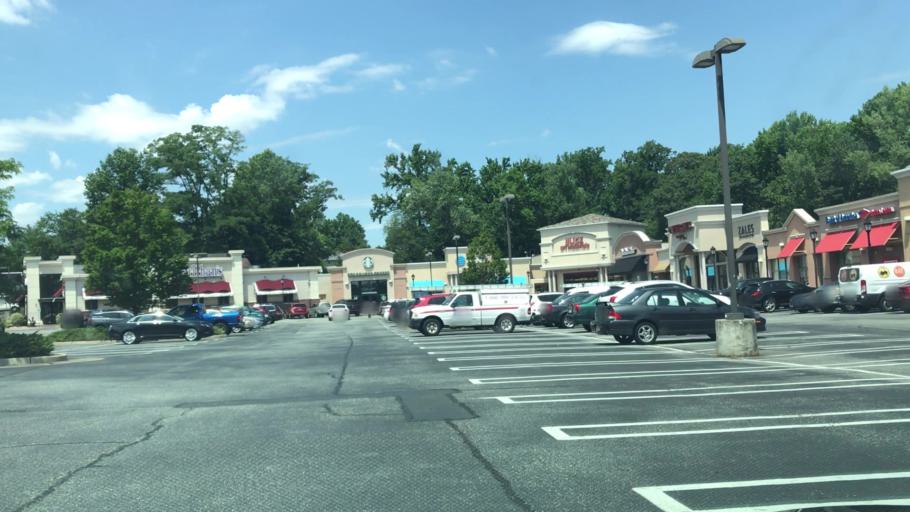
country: US
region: New Jersey
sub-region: Bergen County
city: Rochelle Park
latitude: 40.9196
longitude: -74.0656
